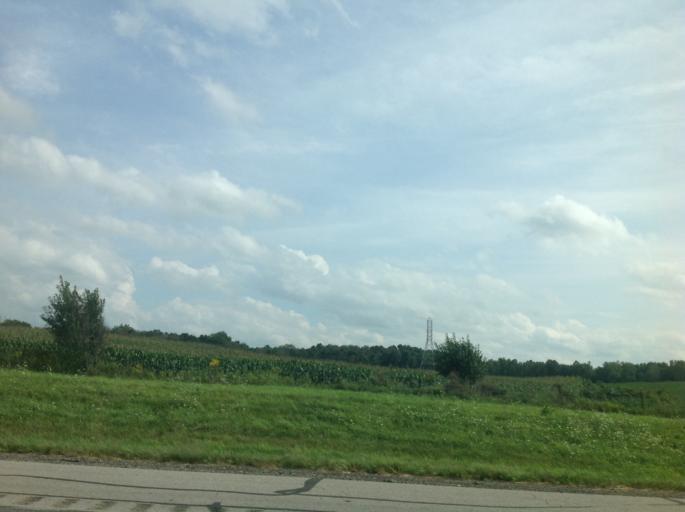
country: US
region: Ohio
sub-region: Ashland County
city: Ashland
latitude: 40.8688
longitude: -82.2357
